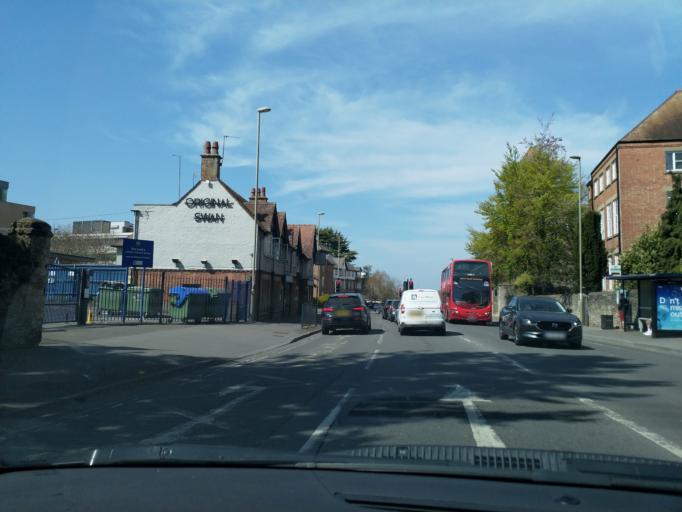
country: GB
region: England
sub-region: Oxfordshire
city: Cowley
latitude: 51.7341
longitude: -1.2110
